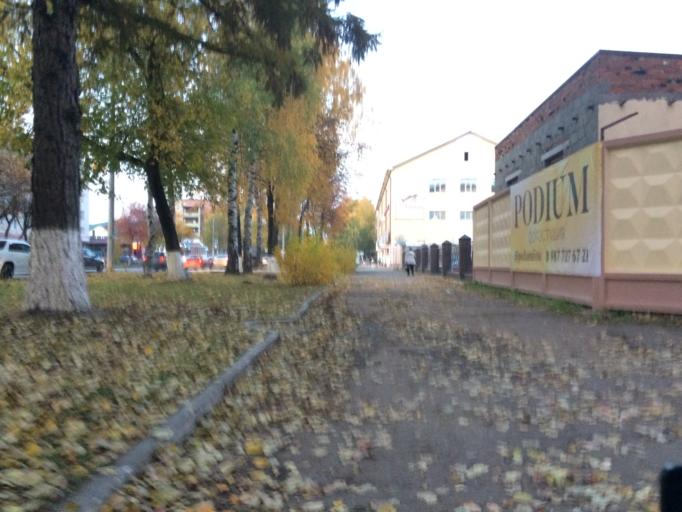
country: RU
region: Mariy-El
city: Yoshkar-Ola
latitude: 56.6153
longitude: 47.8834
